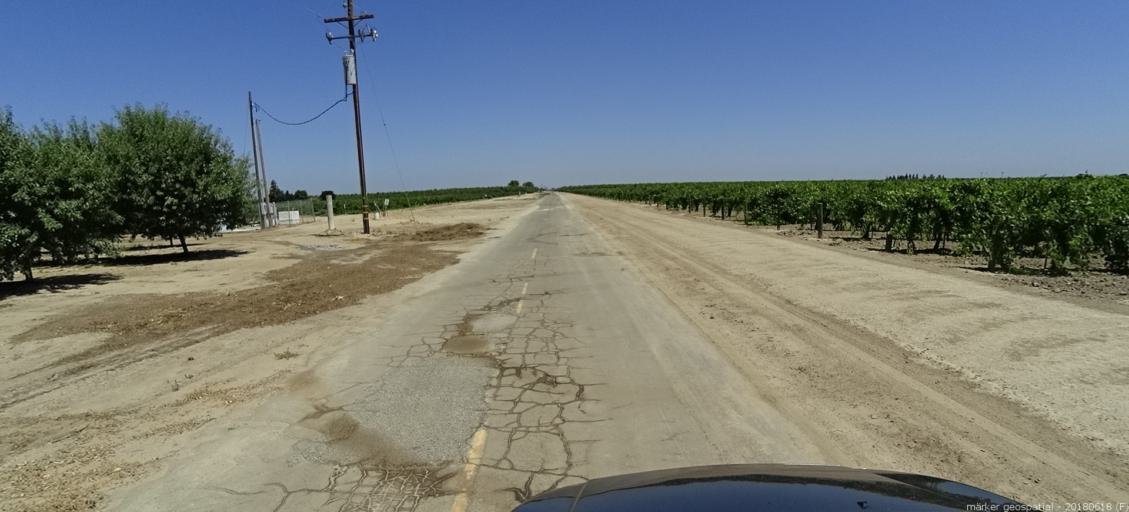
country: US
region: California
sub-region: Madera County
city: Parkwood
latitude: 36.8688
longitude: -120.1013
